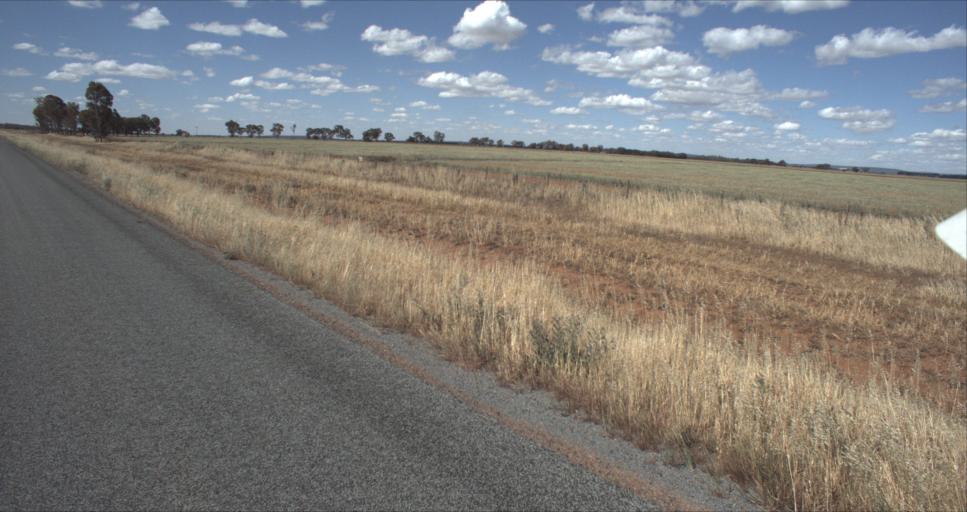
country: AU
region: New South Wales
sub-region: Leeton
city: Leeton
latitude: -34.4635
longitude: 146.2523
